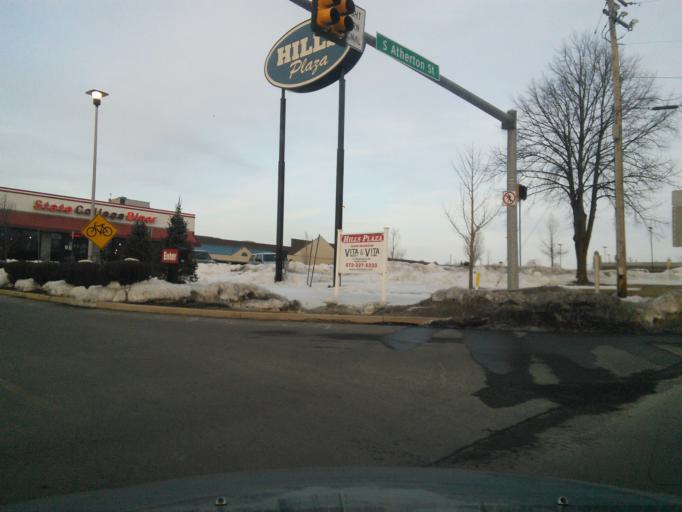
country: US
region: Pennsylvania
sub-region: Centre County
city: State College
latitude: 40.7850
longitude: -77.8323
